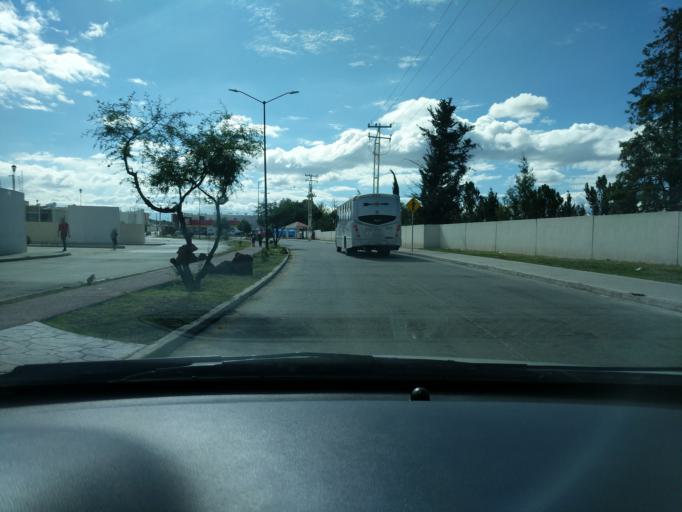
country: MX
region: Queretaro
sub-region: El Marques
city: La Loma
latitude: 20.5880
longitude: -100.2594
